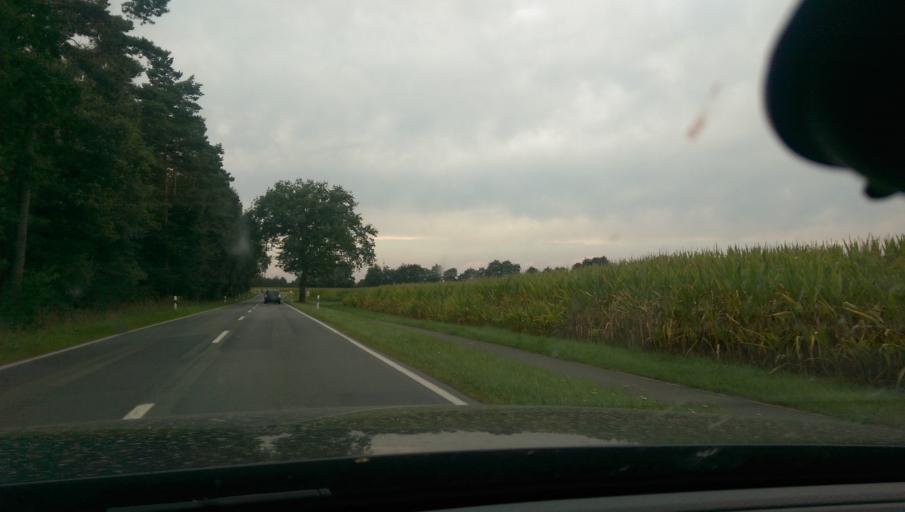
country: DE
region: Lower Saxony
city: Rehburg-Loccum
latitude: 52.4683
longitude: 9.1918
